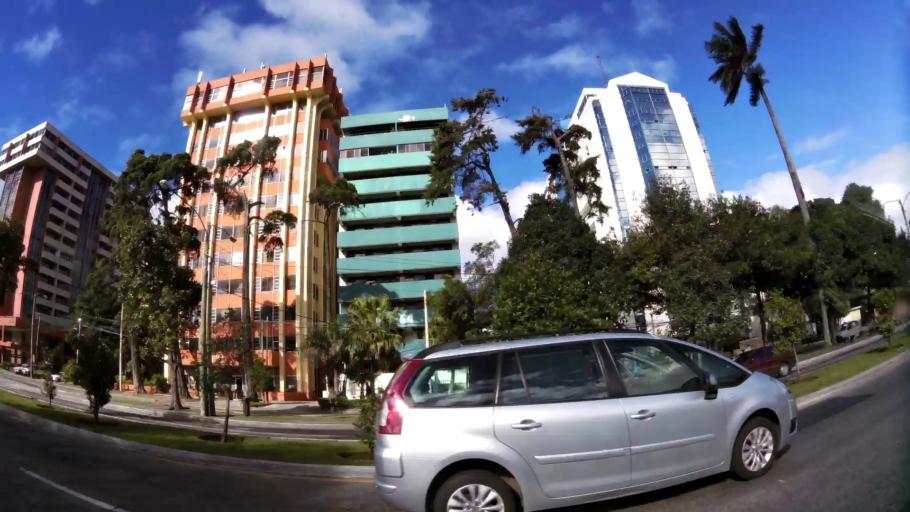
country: GT
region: Guatemala
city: Guatemala City
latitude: 14.6131
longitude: -90.5141
